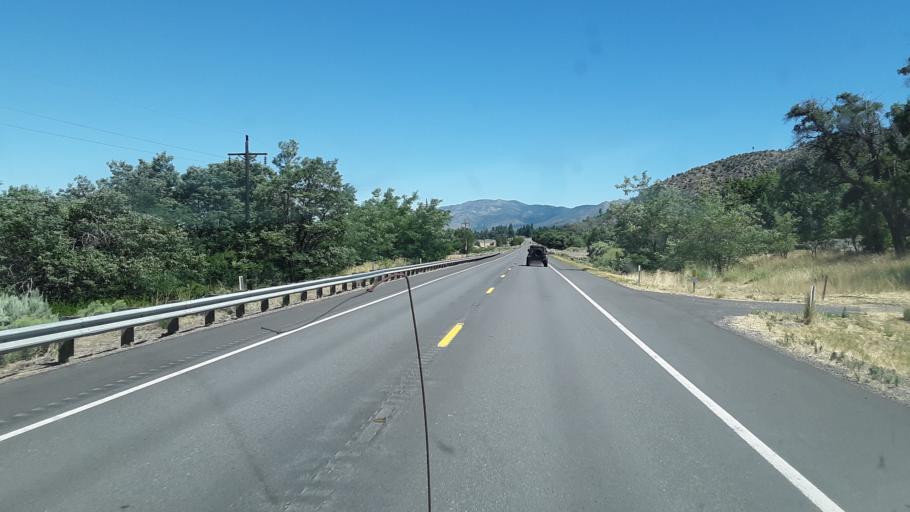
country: US
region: California
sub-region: Lassen County
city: Janesville
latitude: 40.2349
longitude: -120.4469
